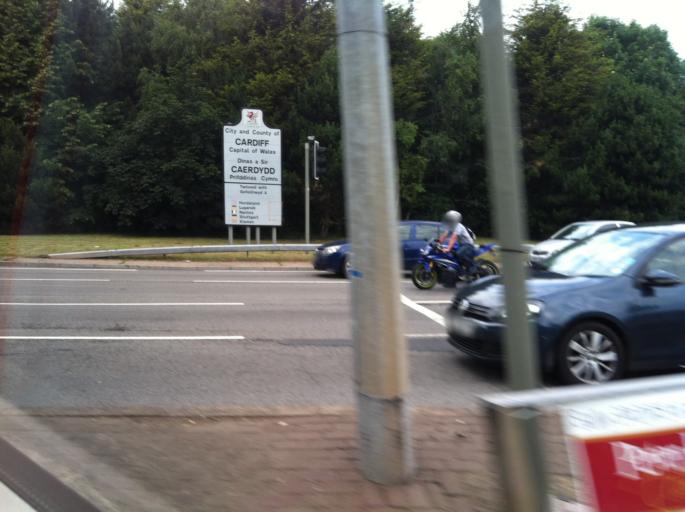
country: GB
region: Wales
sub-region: Cardiff
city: Radyr
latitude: 51.4653
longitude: -3.2709
